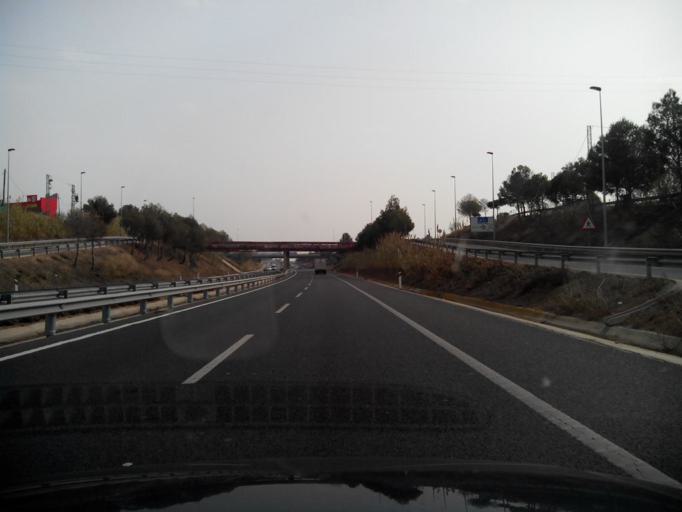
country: ES
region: Catalonia
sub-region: Provincia de Tarragona
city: Reus
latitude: 41.1300
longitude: 1.1185
